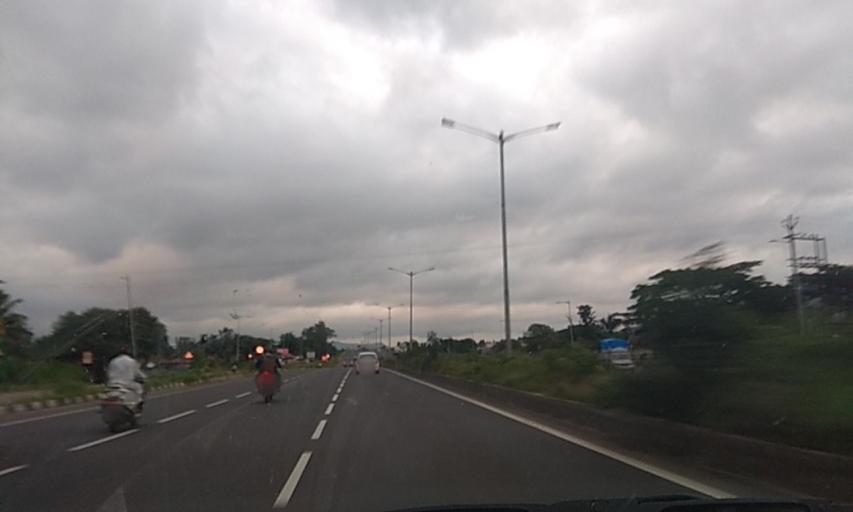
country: IN
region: Maharashtra
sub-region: Satara Division
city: Wai
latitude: 17.8987
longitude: 73.9716
